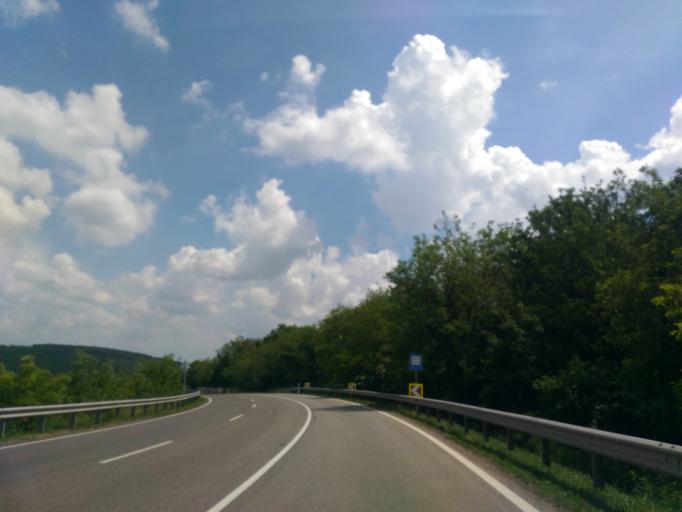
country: HU
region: Baranya
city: Pecs
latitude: 46.1280
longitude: 18.2546
